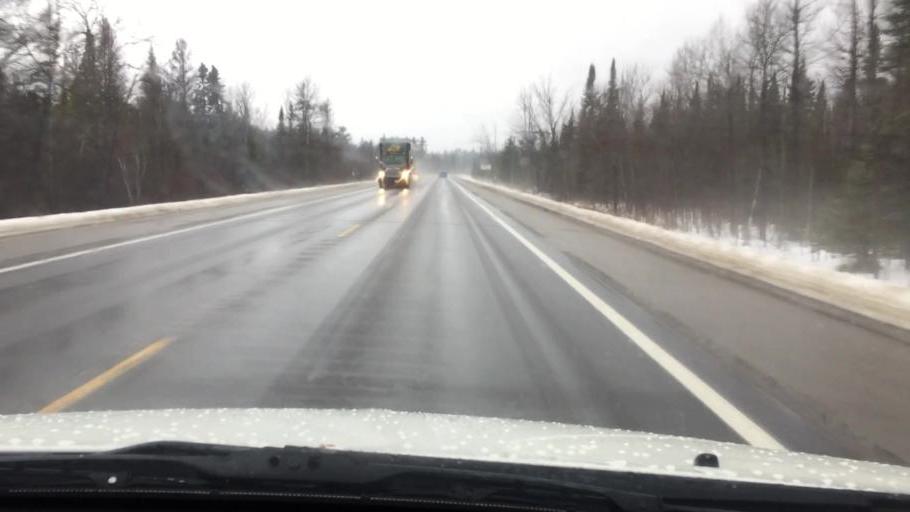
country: US
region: Michigan
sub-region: Kalkaska County
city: Kalkaska
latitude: 44.7060
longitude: -85.1989
